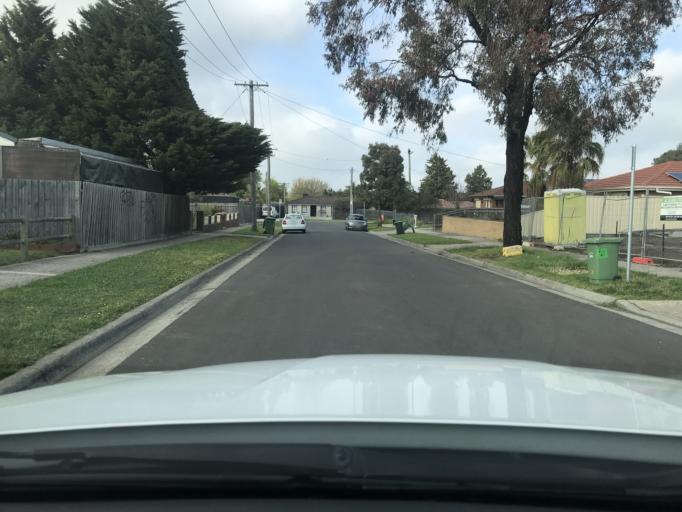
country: AU
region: Victoria
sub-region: Hume
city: Craigieburn
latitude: -37.6016
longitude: 144.9366
